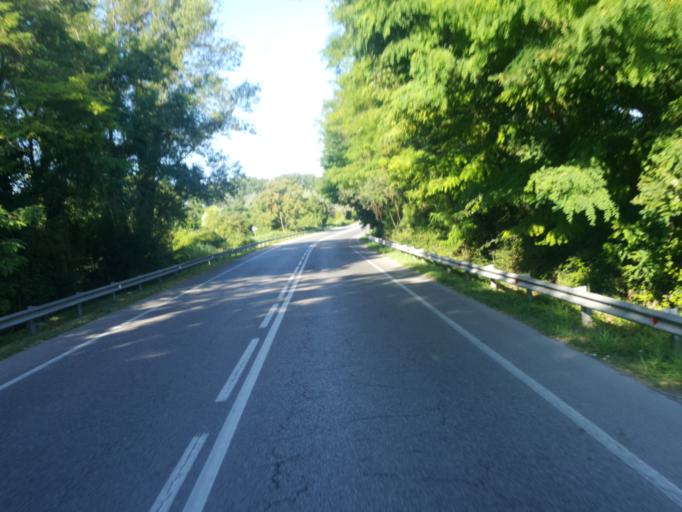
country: IT
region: The Marches
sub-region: Provincia di Pesaro e Urbino
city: Montelabbate
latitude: 43.8468
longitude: 12.7797
